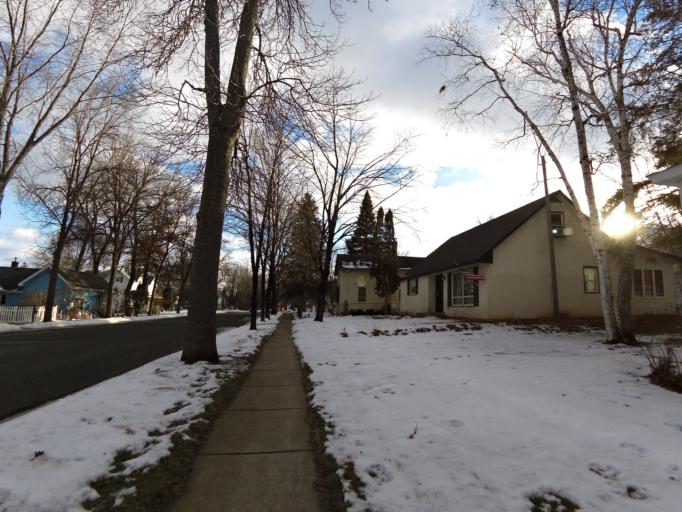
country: US
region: Minnesota
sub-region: Washington County
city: Bayport
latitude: 45.0172
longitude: -92.7825
